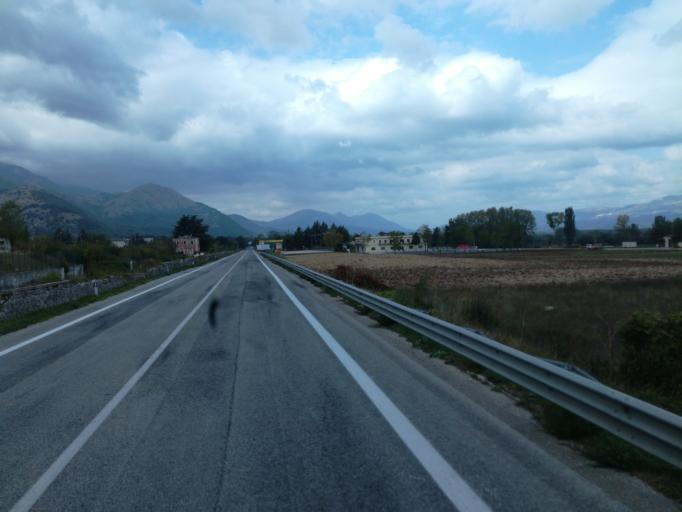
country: IT
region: Molise
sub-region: Provincia di Campobasso
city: Campochiaro
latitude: 41.4734
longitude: 14.5235
